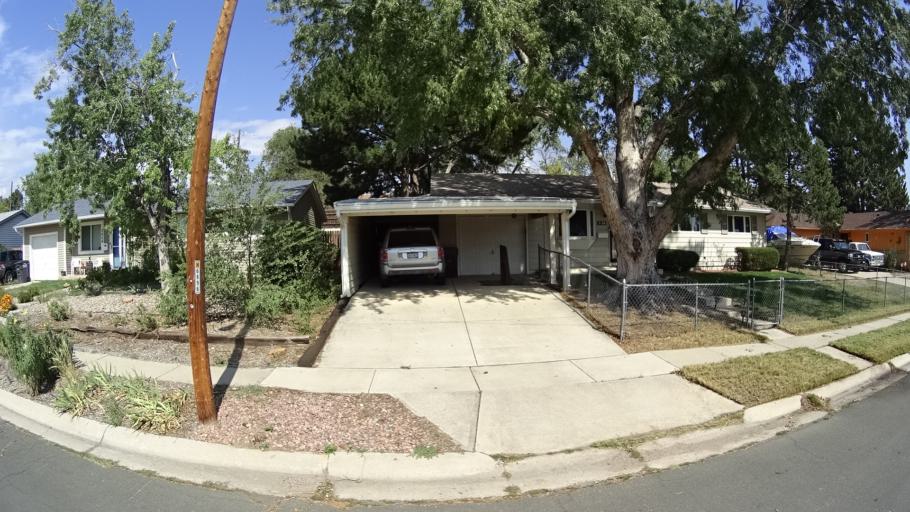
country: US
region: Colorado
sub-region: El Paso County
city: Colorado Springs
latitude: 38.8245
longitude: -104.7839
